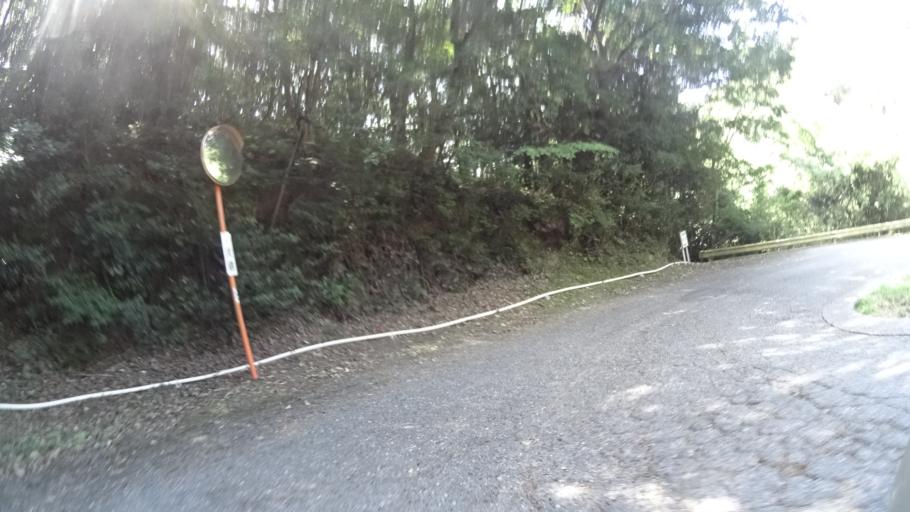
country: JP
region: Yamaguchi
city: Shimonoseki
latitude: 34.1074
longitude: 130.8689
